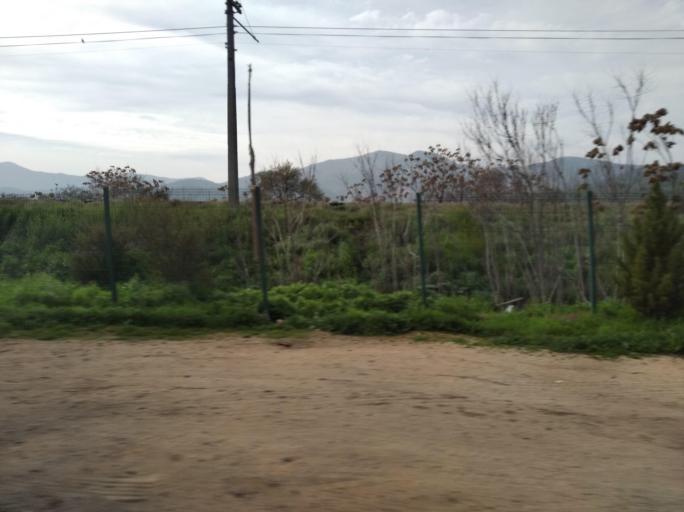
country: CL
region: Santiago Metropolitan
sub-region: Provincia de Chacabuco
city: Lampa
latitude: -33.0964
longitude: -70.9294
